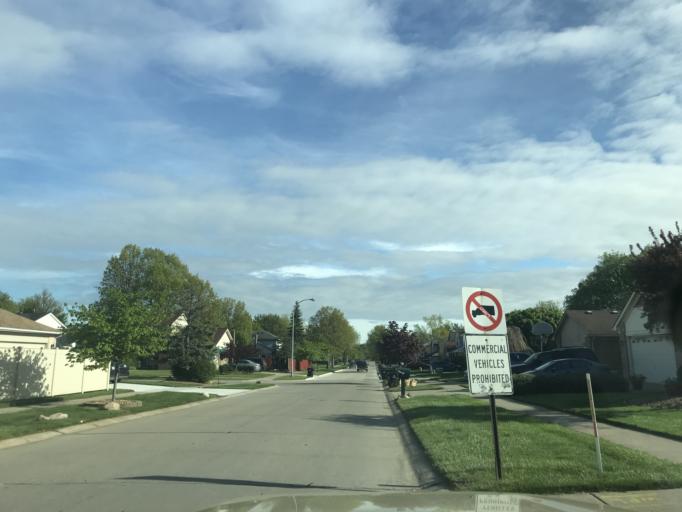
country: US
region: Michigan
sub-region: Wayne County
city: Woodhaven
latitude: 42.1542
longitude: -83.2462
